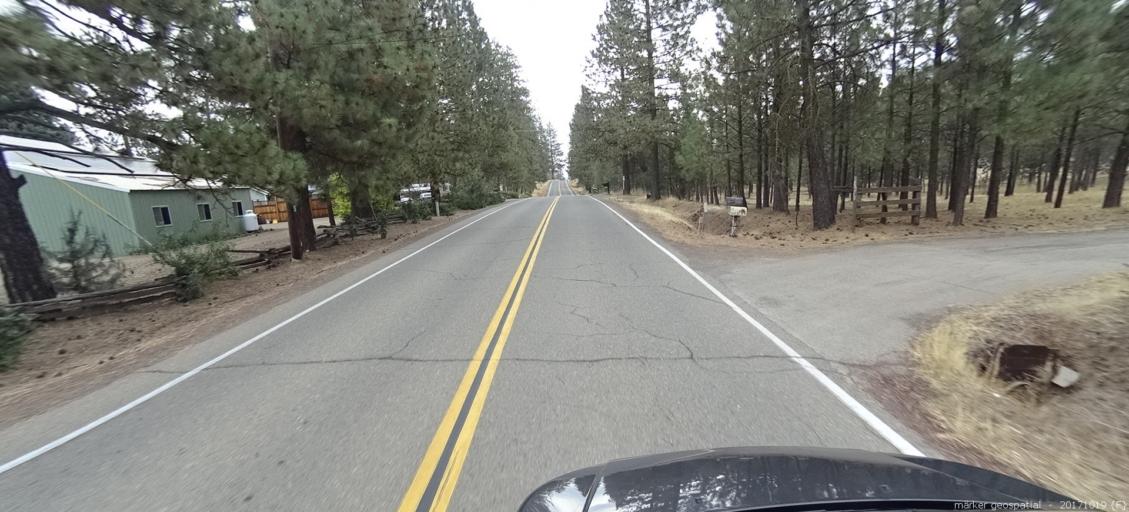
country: US
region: California
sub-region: Shasta County
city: Burney
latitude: 41.0583
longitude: -121.3713
